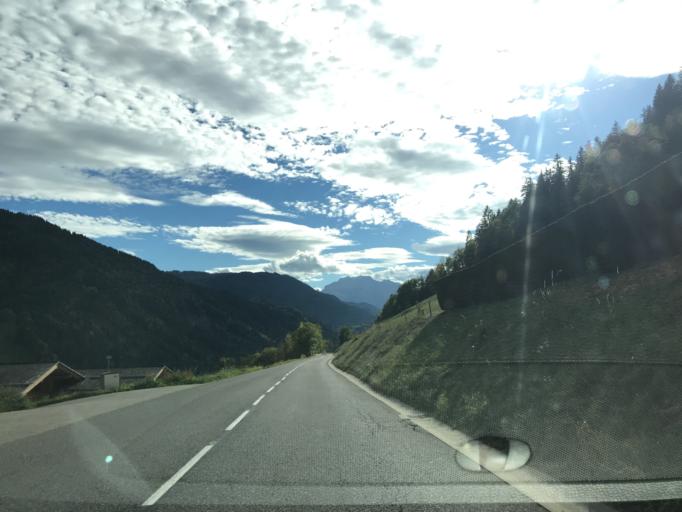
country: FR
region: Rhone-Alpes
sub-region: Departement de la Haute-Savoie
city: Le Grand-Bornand
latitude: 45.9487
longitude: 6.4345
